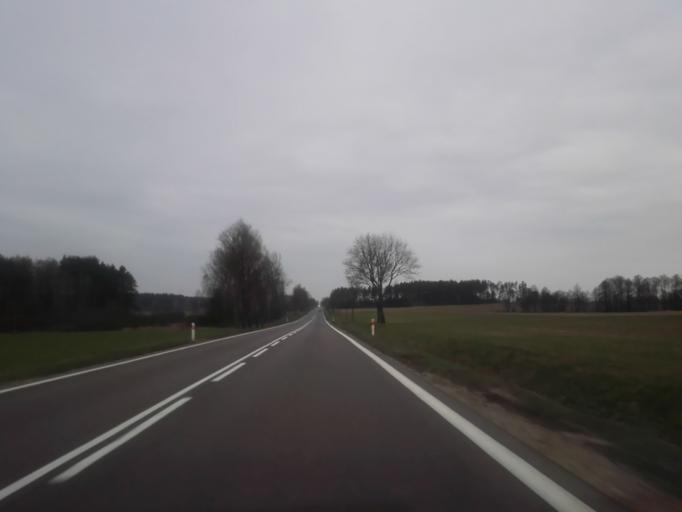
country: PL
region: Podlasie
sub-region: Powiat kolnenski
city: Stawiski
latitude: 53.4750
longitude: 22.2090
